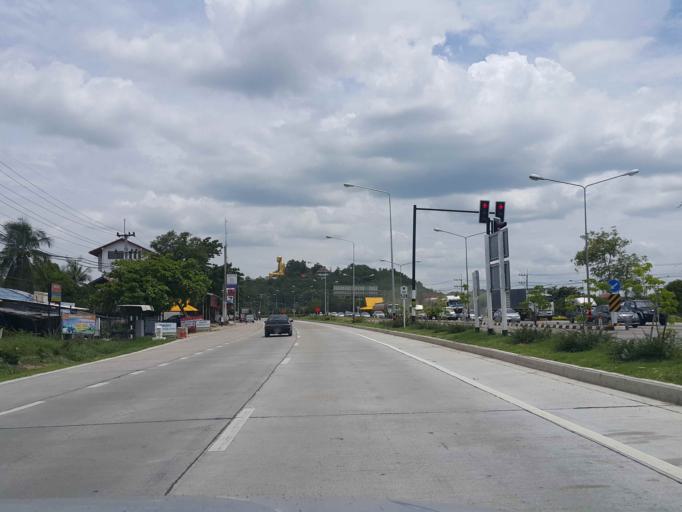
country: TH
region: Lamphun
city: Lamphun
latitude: 18.5528
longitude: 99.0485
